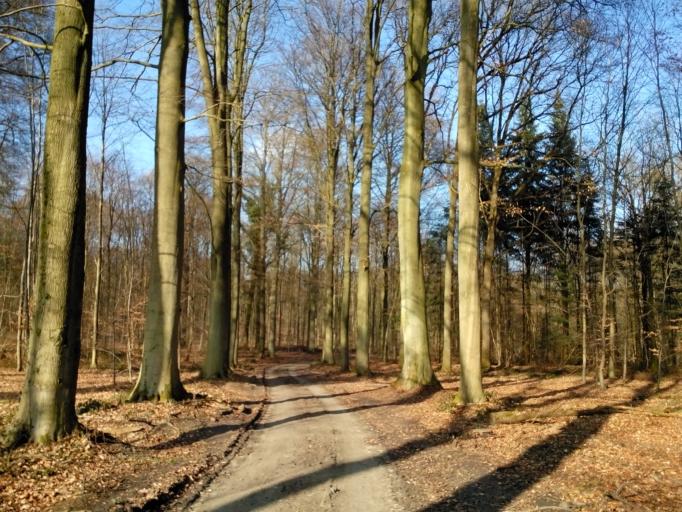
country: BE
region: Flanders
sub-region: Provincie Vlaams-Brabant
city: Oud-Heverlee
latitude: 50.7924
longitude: 4.6959
